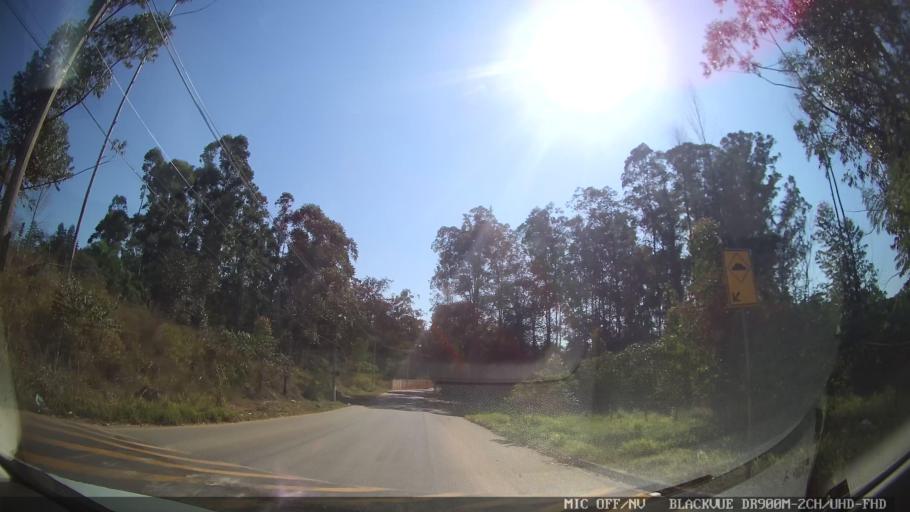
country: BR
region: Sao Paulo
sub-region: Itupeva
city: Itupeva
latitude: -23.1281
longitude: -47.0457
